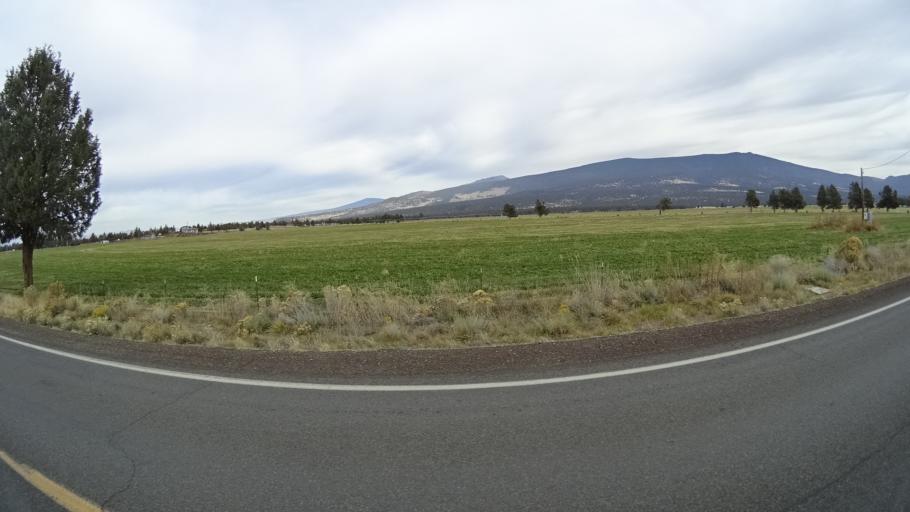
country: US
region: California
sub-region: Siskiyou County
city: Weed
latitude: 41.5977
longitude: -122.3430
